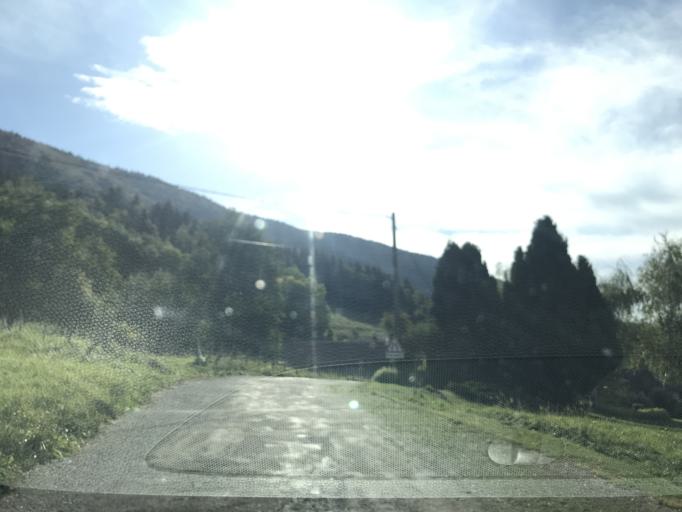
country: FR
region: Rhone-Alpes
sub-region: Departement de la Savoie
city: Novalaise
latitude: 45.6276
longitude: 5.7997
